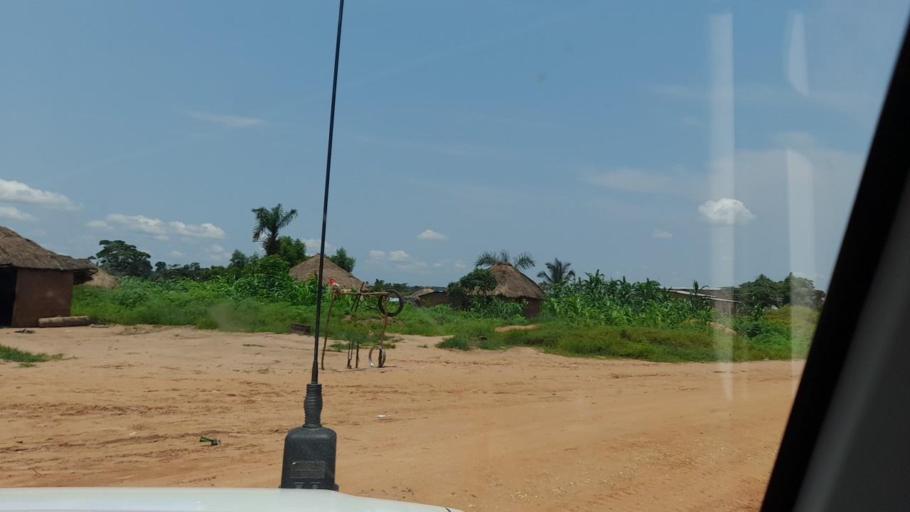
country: CD
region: Kasai-Occidental
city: Kananga
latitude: -5.9523
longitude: 22.2772
